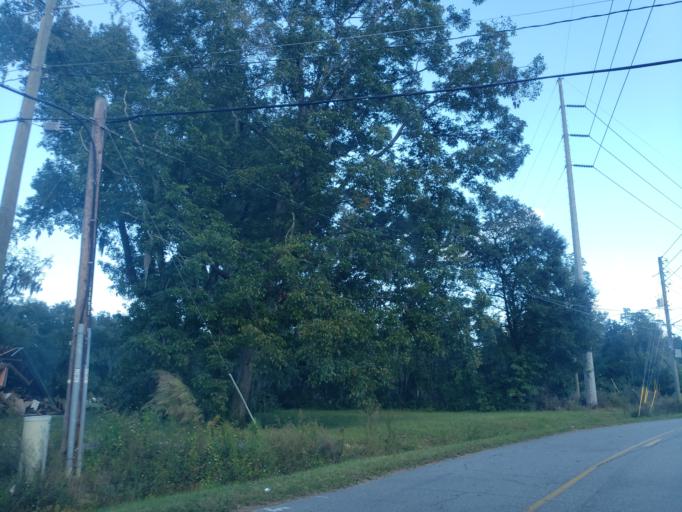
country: US
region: Georgia
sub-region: Chatham County
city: Georgetown
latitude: 31.9895
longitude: -81.2266
